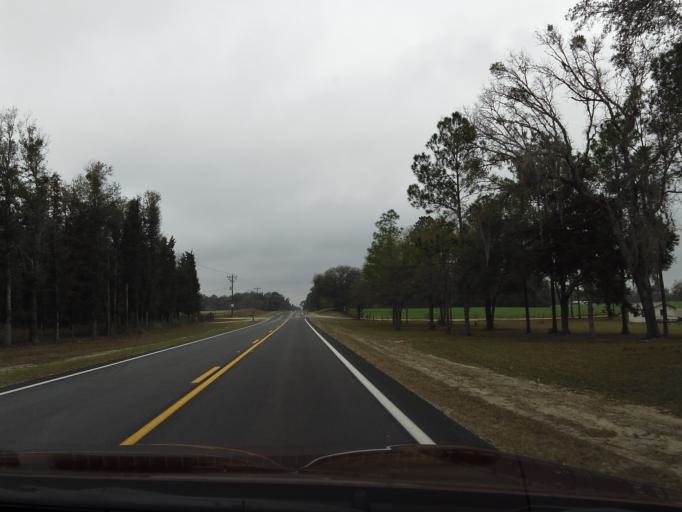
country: US
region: Florida
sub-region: Gilchrist County
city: Trenton
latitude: 29.7963
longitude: -82.8399
